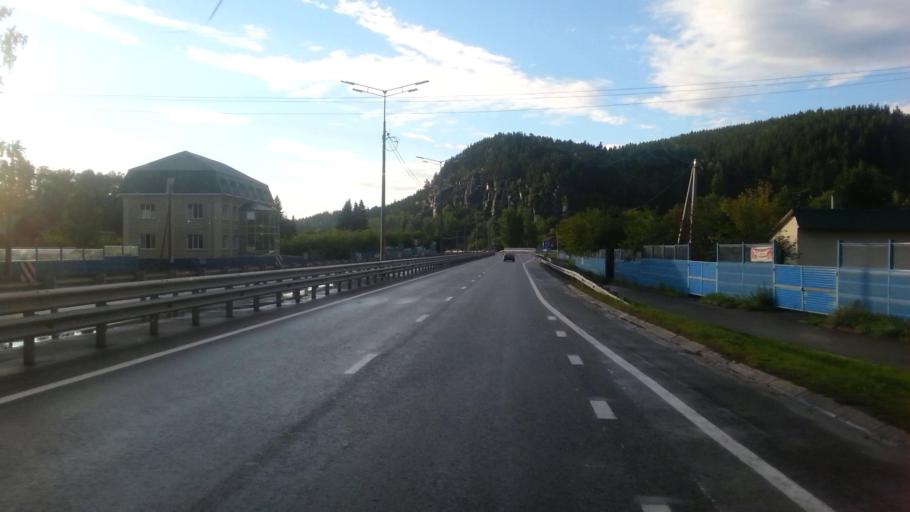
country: RU
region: Altay
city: Souzga
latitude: 51.9158
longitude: 85.8615
